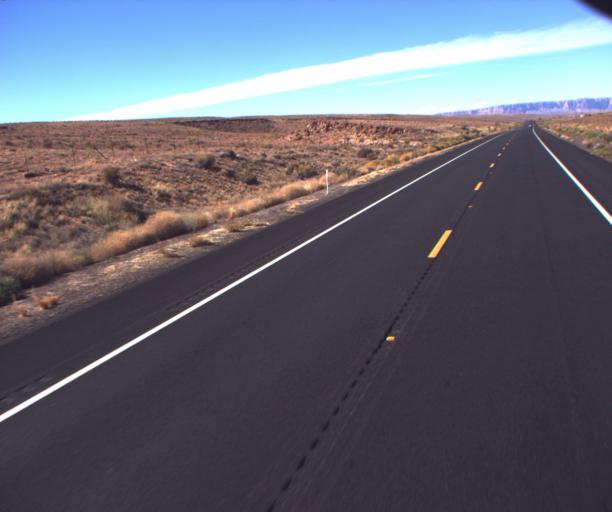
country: US
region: Arizona
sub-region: Coconino County
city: LeChee
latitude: 36.5300
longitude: -111.6061
